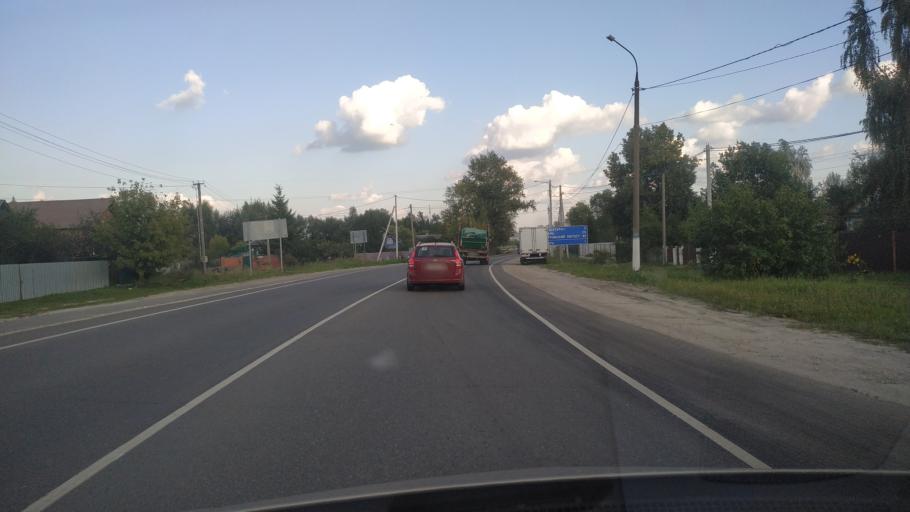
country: RU
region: Moskovskaya
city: Shatura
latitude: 55.5767
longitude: 39.4970
